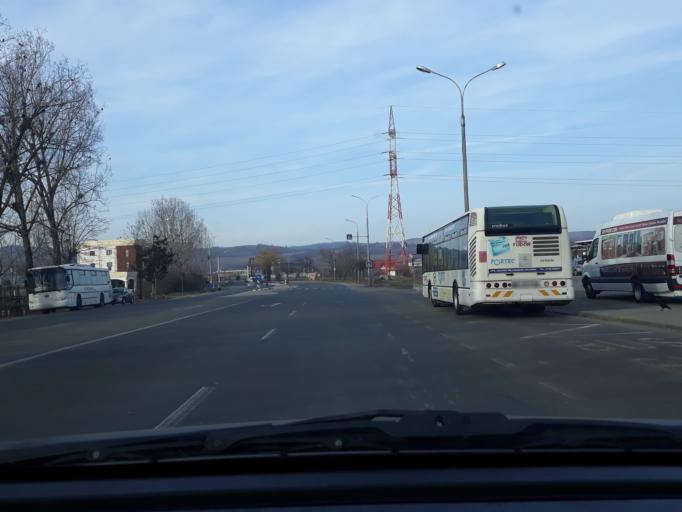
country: RO
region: Salaj
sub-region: Comuna Criseni
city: Criseni
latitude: 47.2203
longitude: 23.0406
